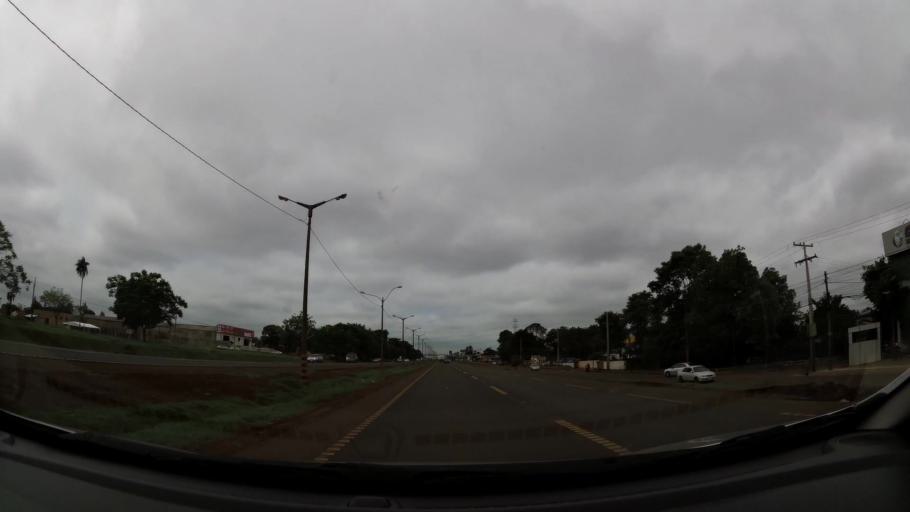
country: PY
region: Alto Parana
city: Ciudad del Este
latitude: -25.4955
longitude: -54.6926
